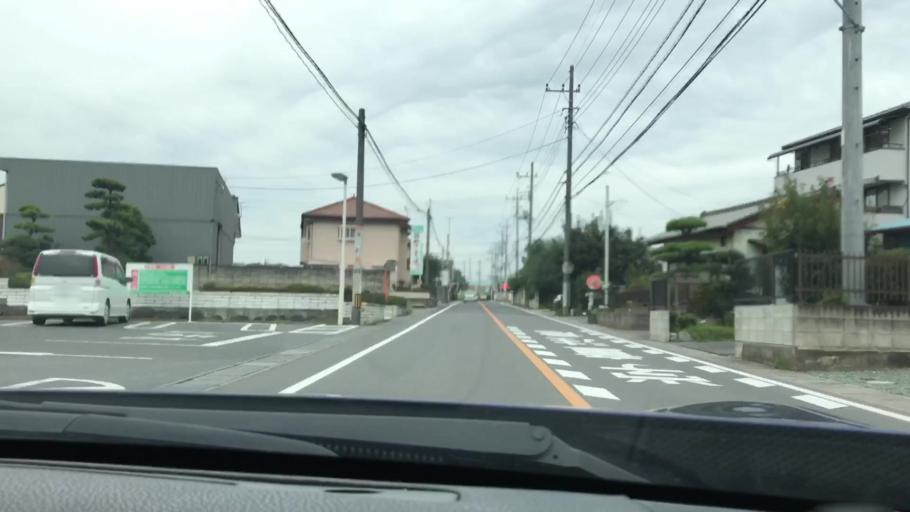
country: JP
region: Gunma
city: Kanekomachi
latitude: 36.3956
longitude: 139.0043
